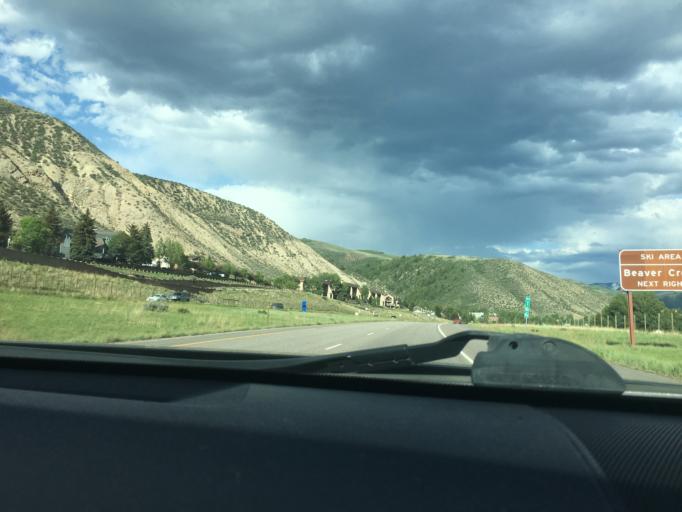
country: US
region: Colorado
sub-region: Eagle County
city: Avon
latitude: 39.6403
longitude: -106.5328
